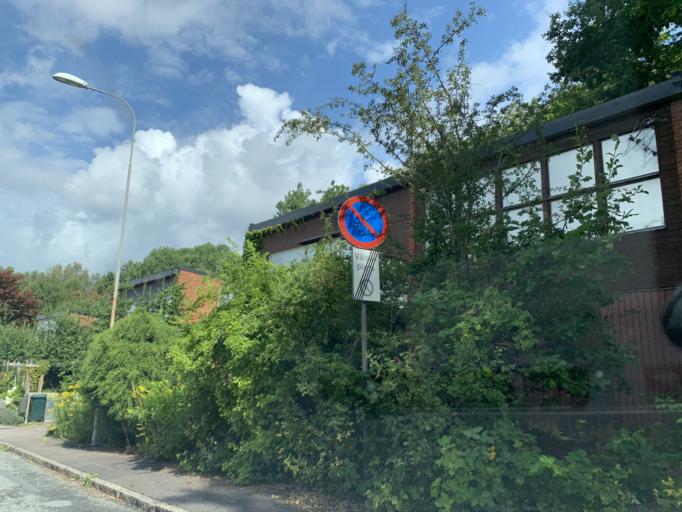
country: SE
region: Vaestra Goetaland
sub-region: Goteborg
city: Eriksbo
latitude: 57.7450
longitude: 12.0558
